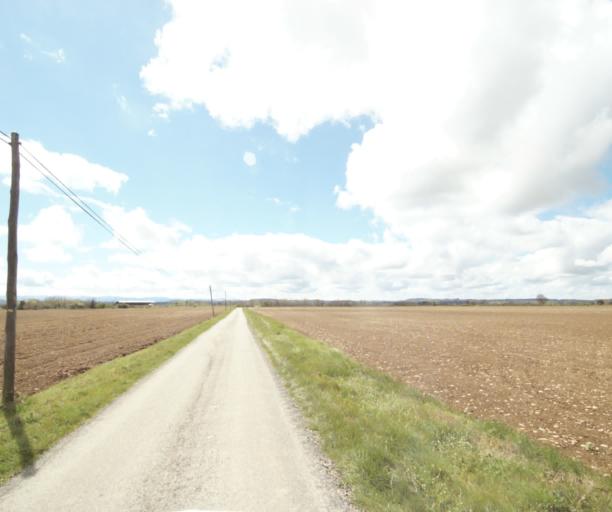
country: FR
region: Midi-Pyrenees
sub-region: Departement de l'Ariege
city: Saverdun
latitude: 43.2497
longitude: 1.6062
